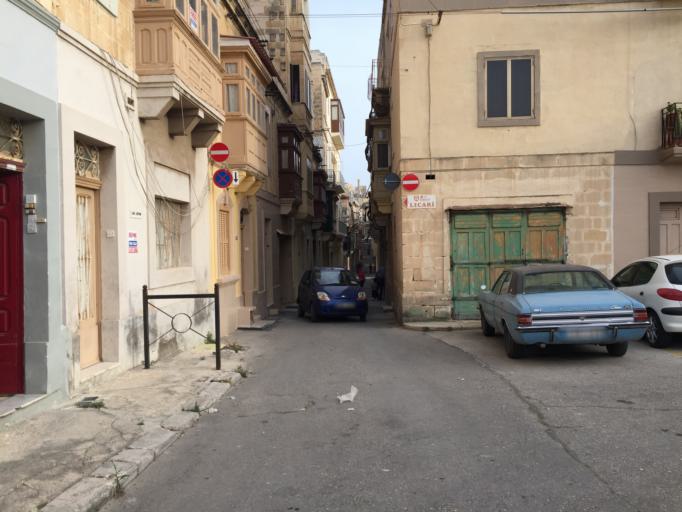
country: MT
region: L-Isla
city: Senglea
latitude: 35.8829
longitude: 14.5188
